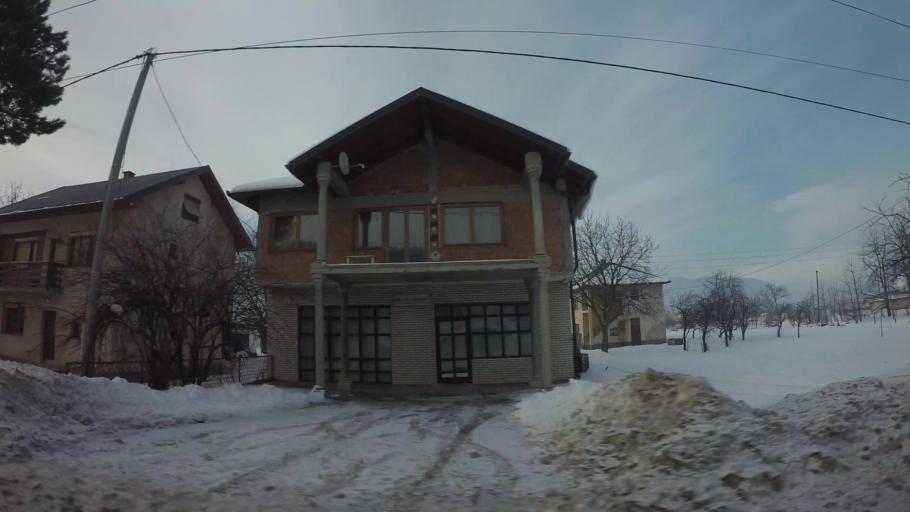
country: BA
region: Federation of Bosnia and Herzegovina
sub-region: Kanton Sarajevo
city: Sarajevo
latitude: 43.8060
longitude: 18.3458
